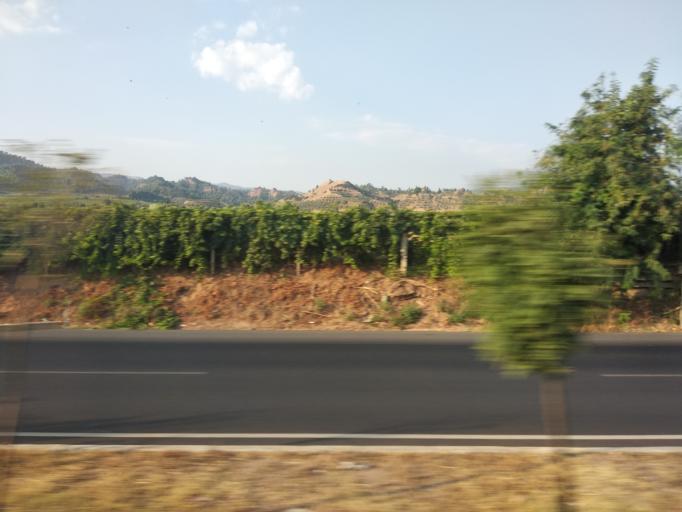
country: TR
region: Manisa
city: Ahmetli
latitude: 38.5044
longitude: 28.0068
